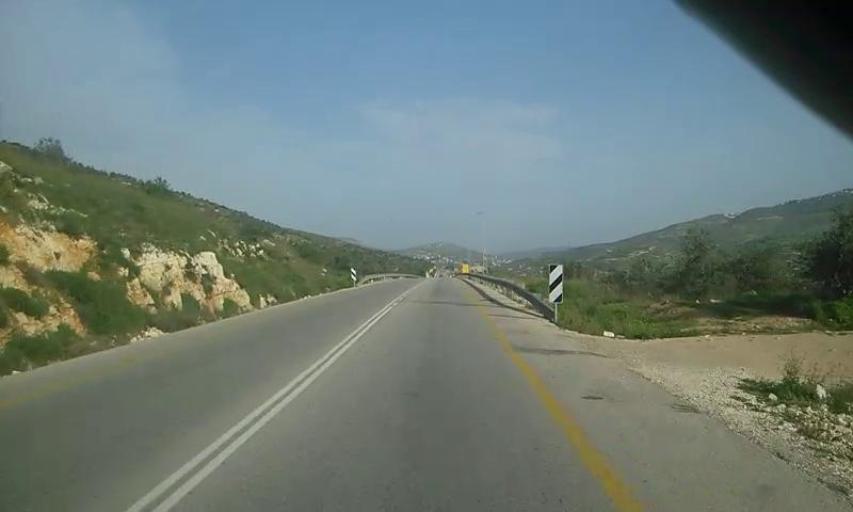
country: PS
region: West Bank
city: Till
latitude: 32.1897
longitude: 35.2093
